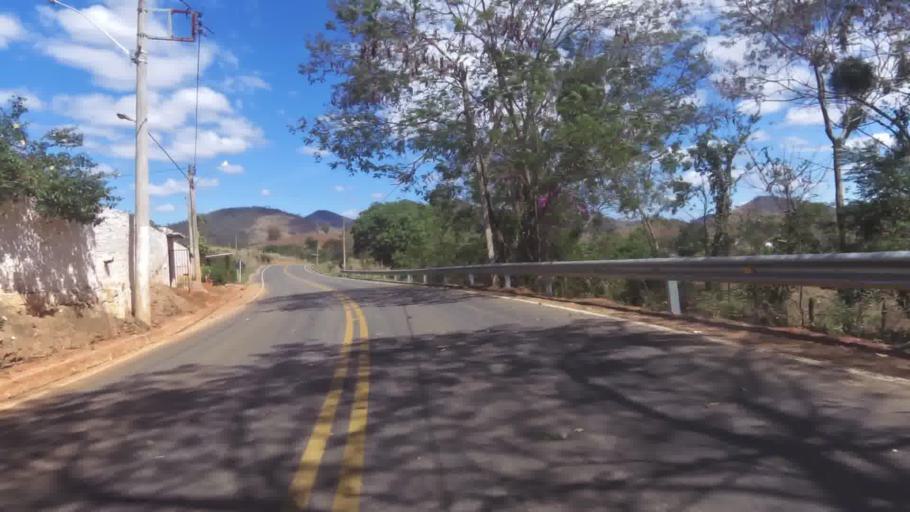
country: BR
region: Espirito Santo
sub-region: Cachoeiro De Itapemirim
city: Cachoeiro de Itapemirim
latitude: -20.9126
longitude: -41.2142
